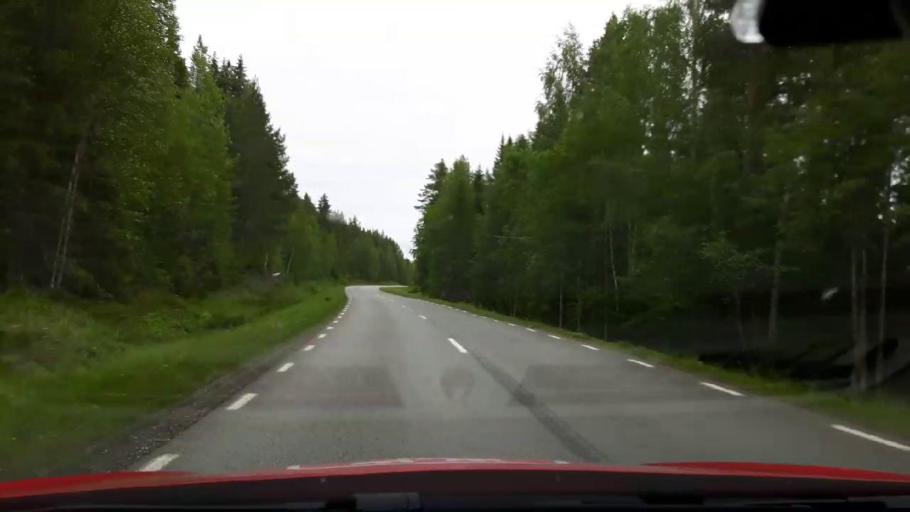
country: SE
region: Jaemtland
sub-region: Stroemsunds Kommun
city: Stroemsund
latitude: 63.4078
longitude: 15.6189
